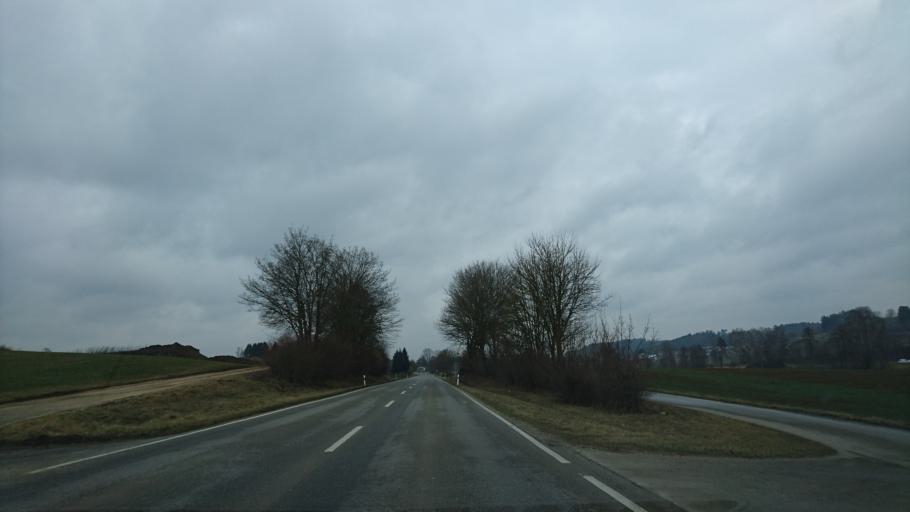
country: DE
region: Bavaria
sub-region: Swabia
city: Altenmunster
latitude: 48.4515
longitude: 10.5876
